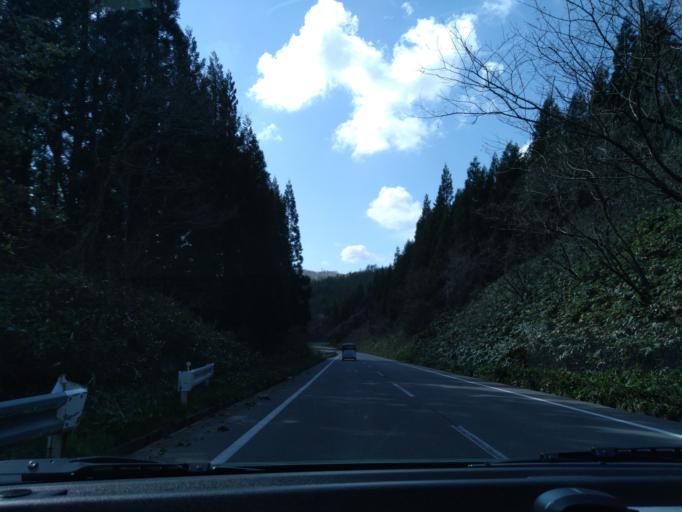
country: JP
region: Akita
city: Akita
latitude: 39.6948
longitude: 140.2391
